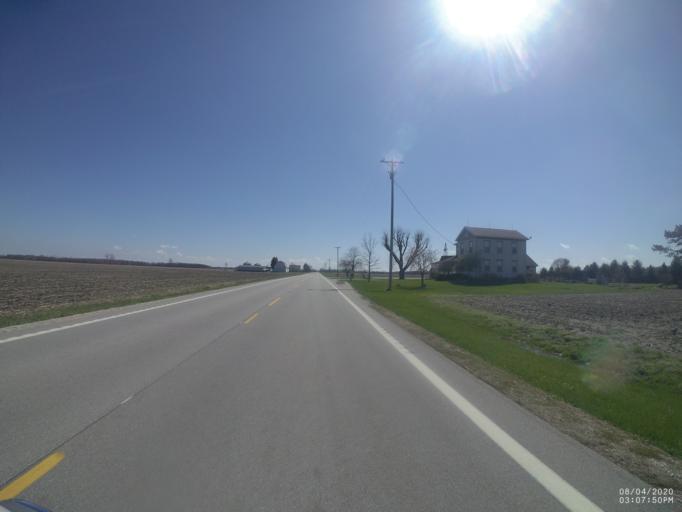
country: US
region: Ohio
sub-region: Sandusky County
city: Stony Prairie
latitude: 41.2920
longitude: -83.2358
